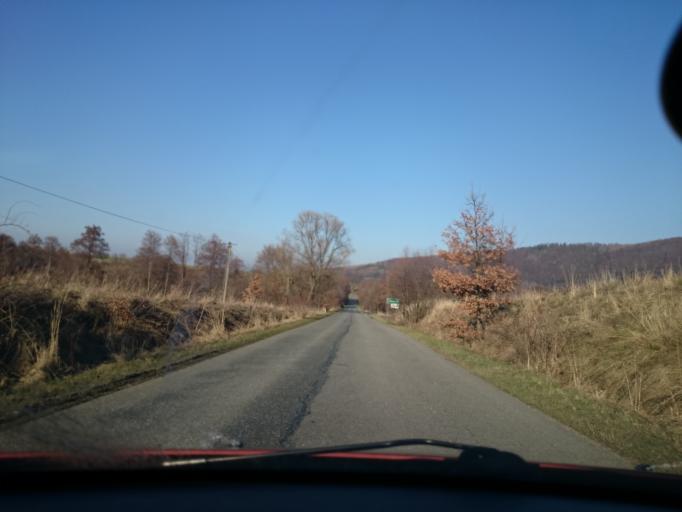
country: PL
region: Lower Silesian Voivodeship
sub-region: Powiat klodzki
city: Bystrzyca Klodzka
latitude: 50.3581
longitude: 16.6296
